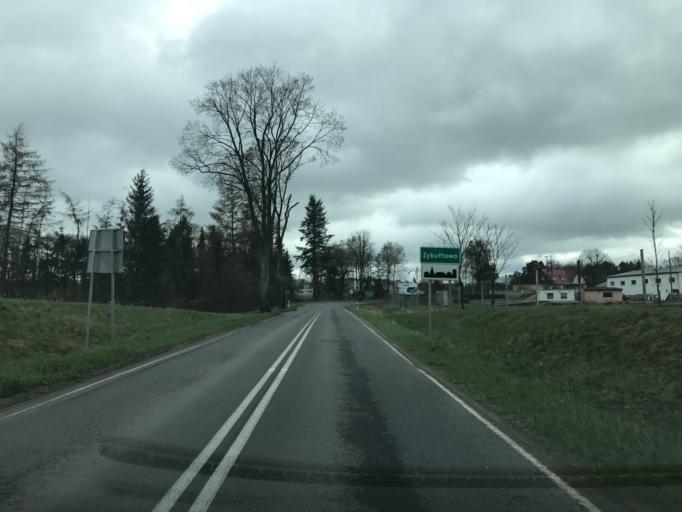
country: PL
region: Warmian-Masurian Voivodeship
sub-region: Powiat ostrodzki
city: Gierzwald
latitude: 53.5017
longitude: 20.1722
